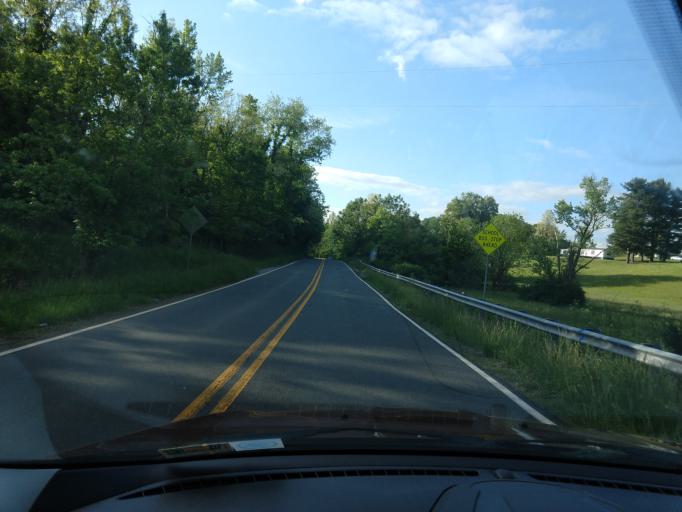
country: US
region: Virginia
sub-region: Wythe County
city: Wytheville
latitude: 36.8994
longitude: -80.9702
